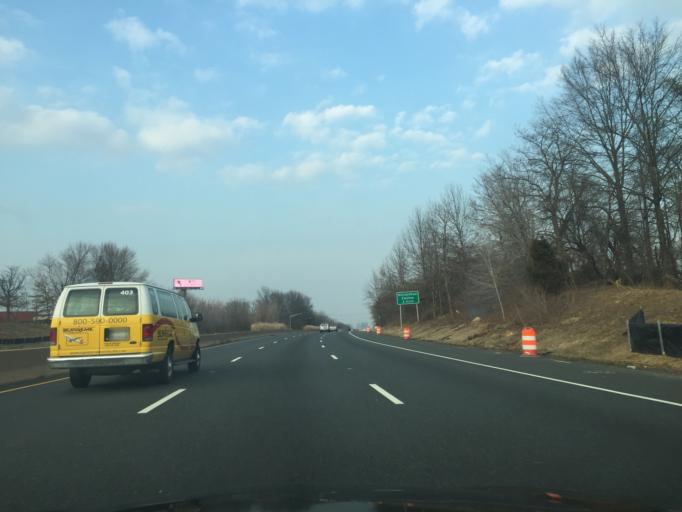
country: US
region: Maryland
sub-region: Baltimore County
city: Lansdowne
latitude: 39.2472
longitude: -76.6460
